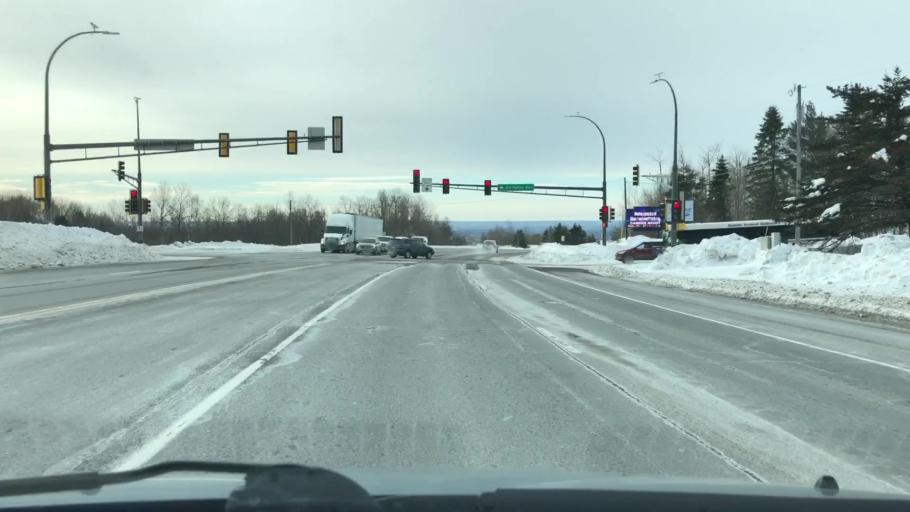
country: US
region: Minnesota
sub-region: Saint Louis County
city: Duluth
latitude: 46.7831
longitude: -92.1389
